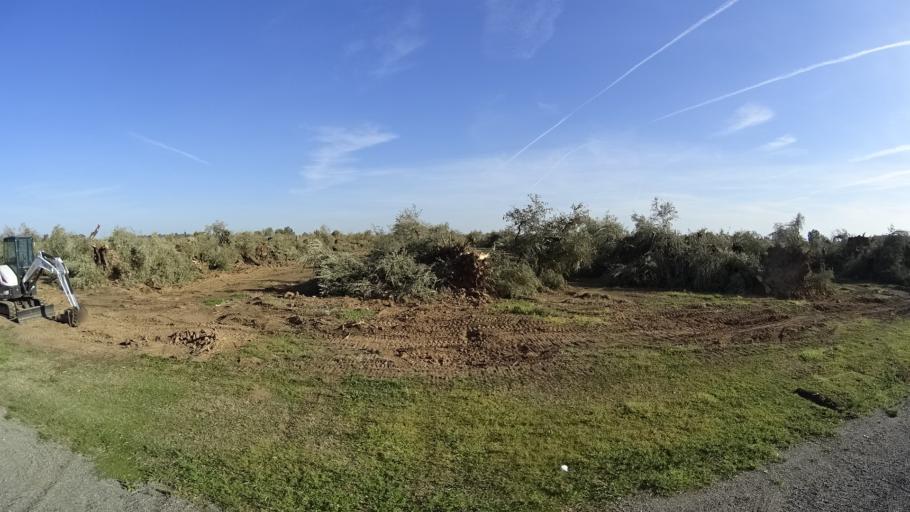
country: US
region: California
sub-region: Glenn County
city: Orland
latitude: 39.7261
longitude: -122.2317
